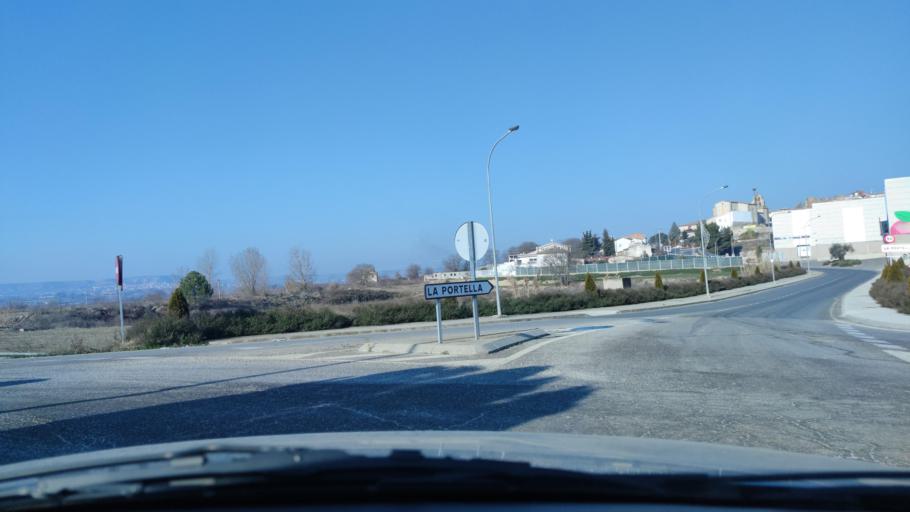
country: ES
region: Catalonia
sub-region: Provincia de Lleida
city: Albesa
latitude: 41.7362
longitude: 0.6432
